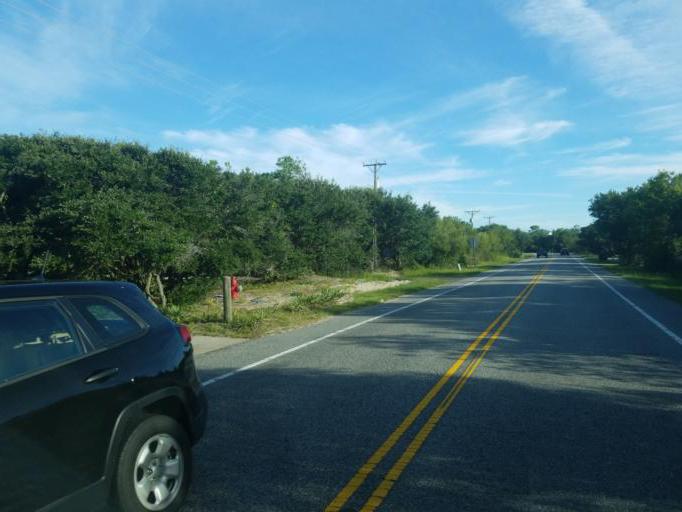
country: US
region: North Carolina
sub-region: Dare County
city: Southern Shores
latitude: 36.2956
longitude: -75.8028
